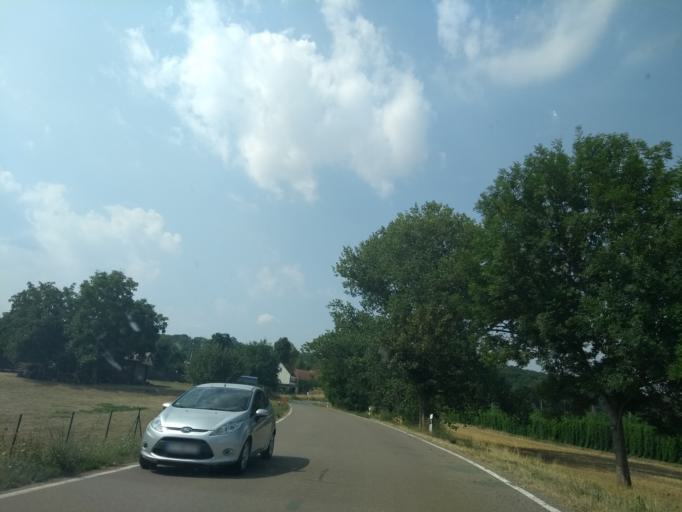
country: DE
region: Saxony-Anhalt
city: Kretzschau
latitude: 51.0236
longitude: 12.0857
